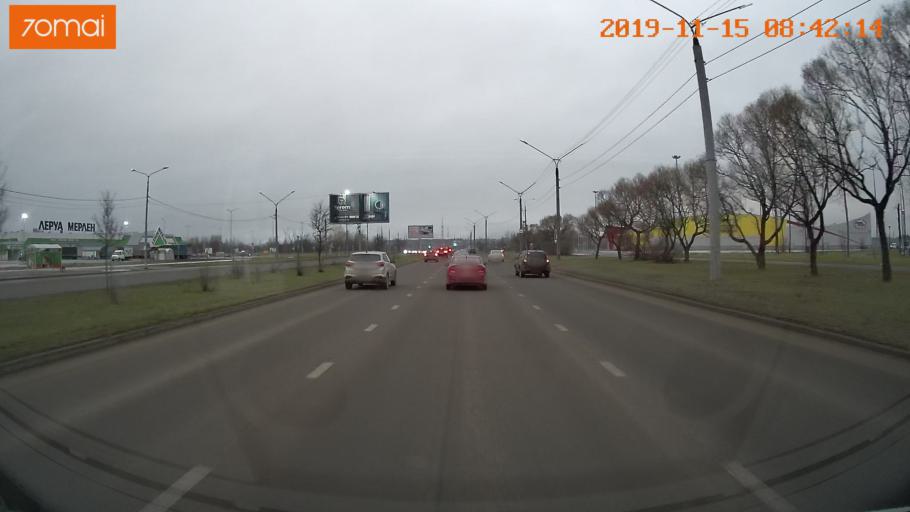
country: RU
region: Vologda
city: Cherepovets
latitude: 59.1015
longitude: 37.9090
